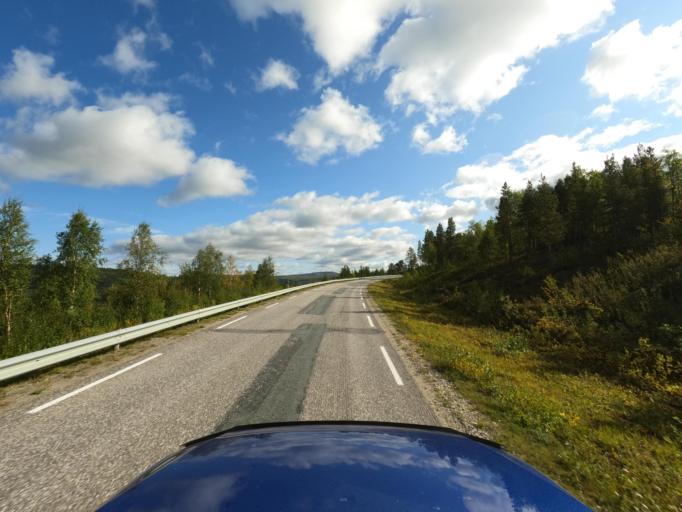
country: NO
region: Finnmark Fylke
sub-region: Karasjok
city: Karasjohka
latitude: 69.4352
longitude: 25.7076
